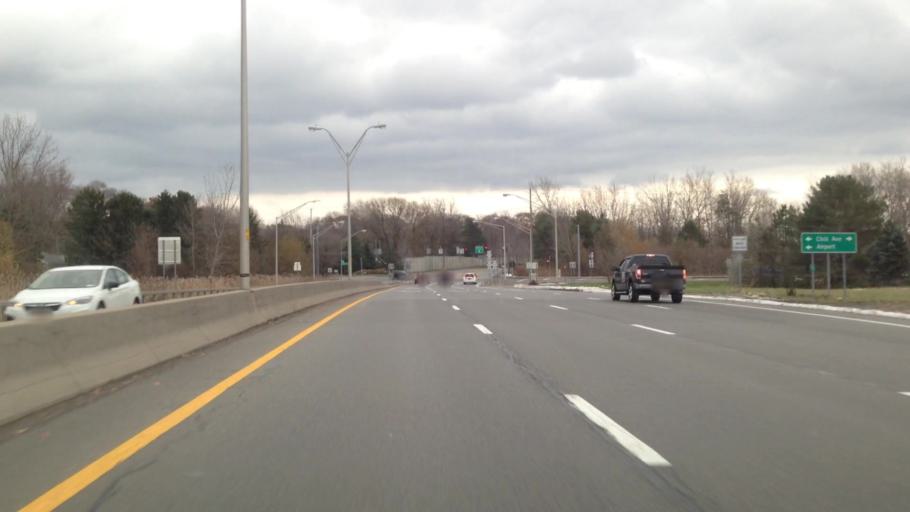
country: US
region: New York
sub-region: Monroe County
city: North Gates
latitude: 43.1270
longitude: -77.7036
